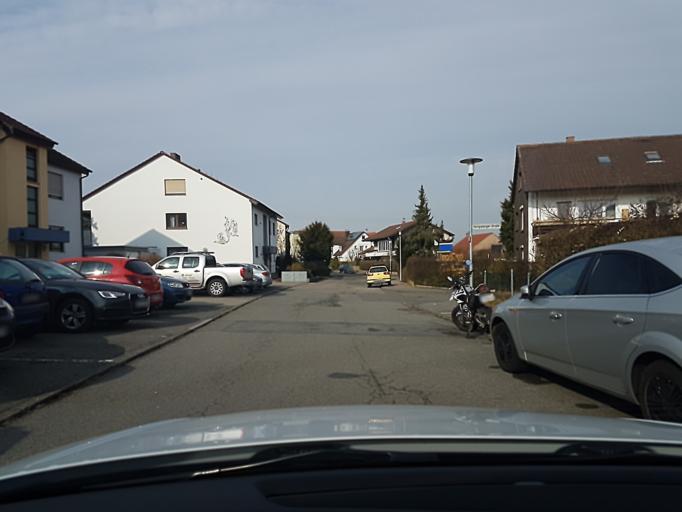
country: DE
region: Baden-Wuerttemberg
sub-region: Regierungsbezirk Stuttgart
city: Leingarten
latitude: 49.1414
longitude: 9.1295
